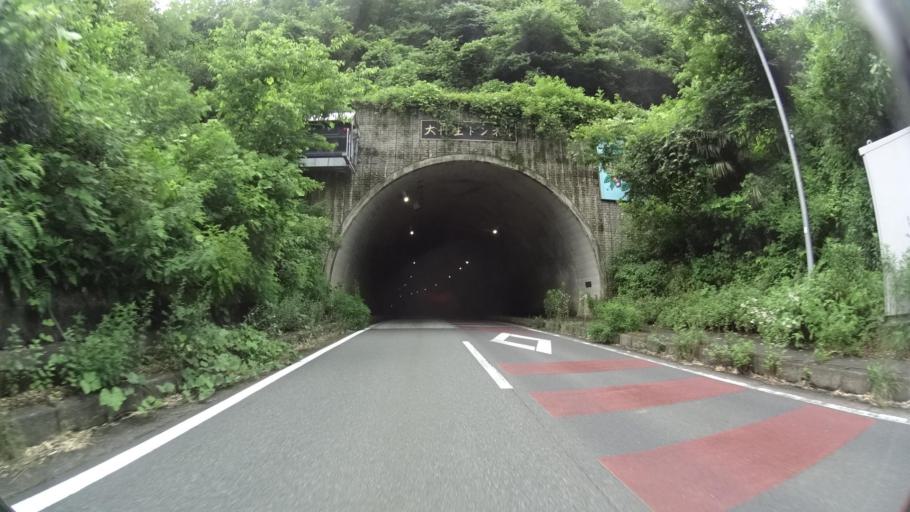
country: JP
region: Kyoto
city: Maizuru
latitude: 35.5236
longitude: 135.3454
